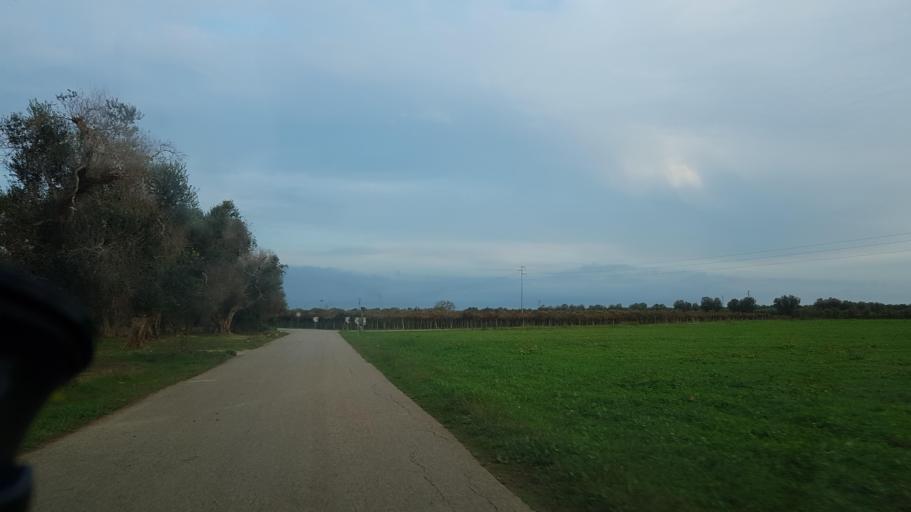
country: IT
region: Apulia
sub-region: Provincia di Brindisi
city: Latiano
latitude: 40.5388
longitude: 17.7450
